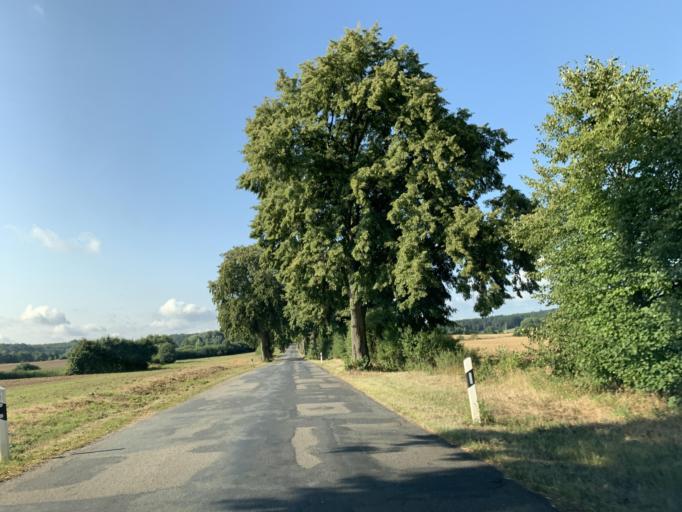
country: DE
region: Mecklenburg-Vorpommern
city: Blankensee
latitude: 53.3384
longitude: 13.3468
